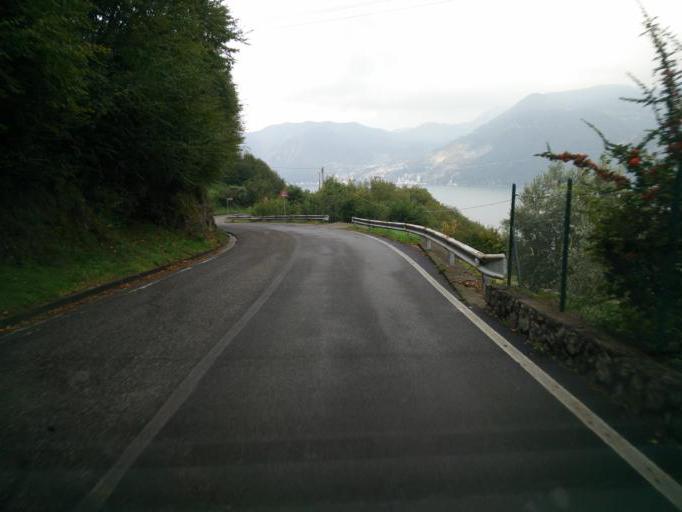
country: IT
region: Lombardy
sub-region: Provincia di Brescia
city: Marone
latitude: 45.7428
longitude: 10.1013
